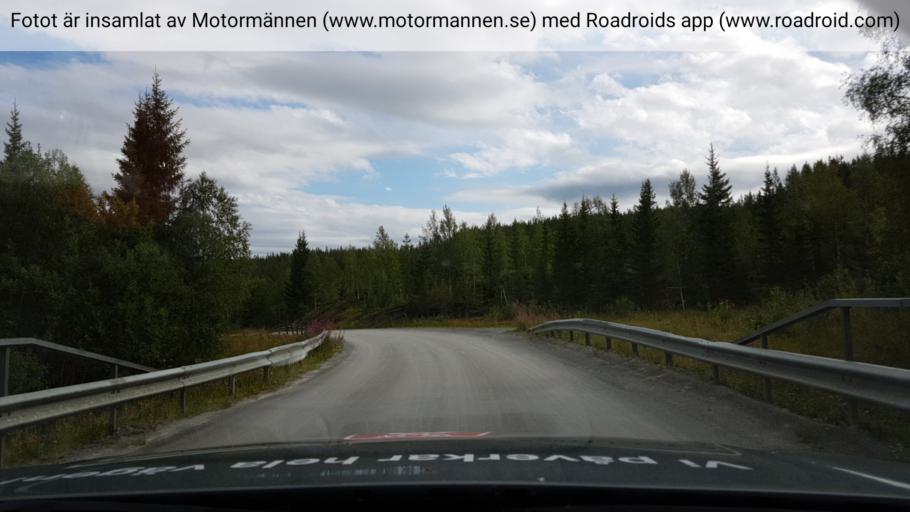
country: SE
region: Jaemtland
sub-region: Krokoms Kommun
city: Valla
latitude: 63.6629
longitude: 13.7330
